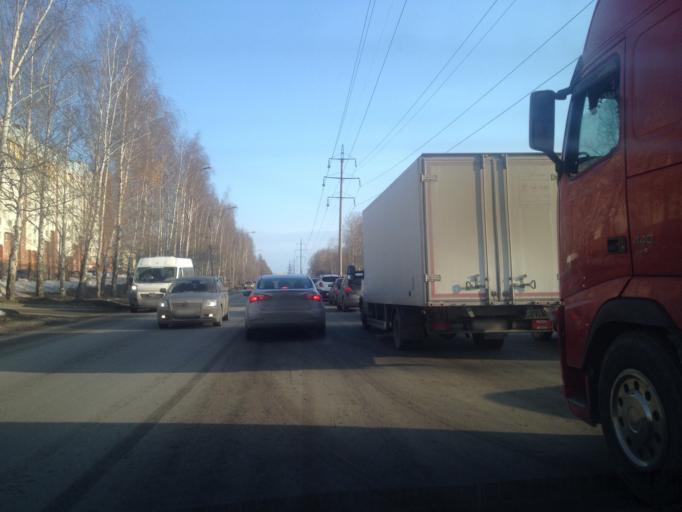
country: RU
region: Sverdlovsk
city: Sovkhoznyy
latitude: 56.7778
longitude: 60.5986
